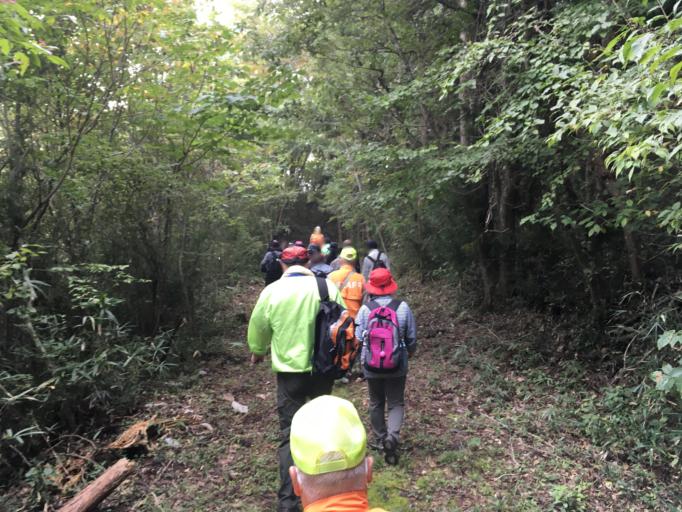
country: JP
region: Iwate
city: Ichinoseki
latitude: 38.8869
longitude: 141.0859
